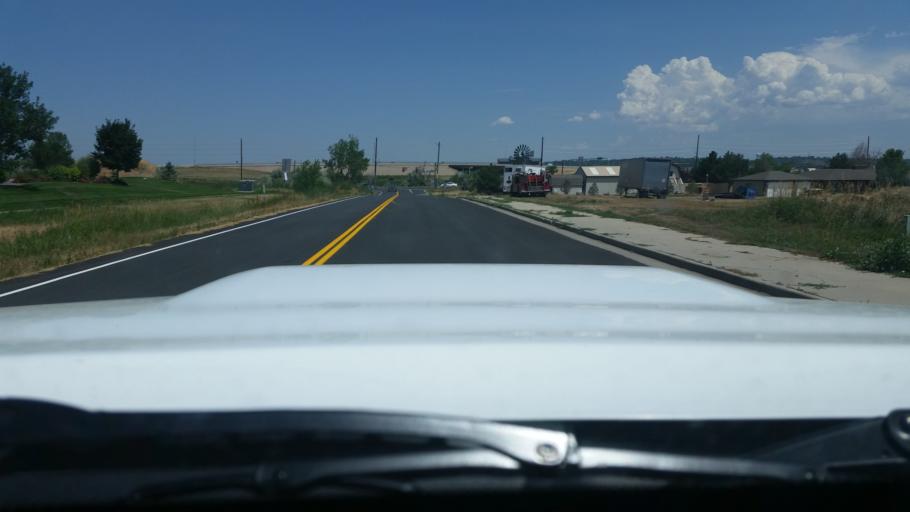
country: US
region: Colorado
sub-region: Broomfield County
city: Broomfield
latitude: 39.8925
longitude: -105.0838
